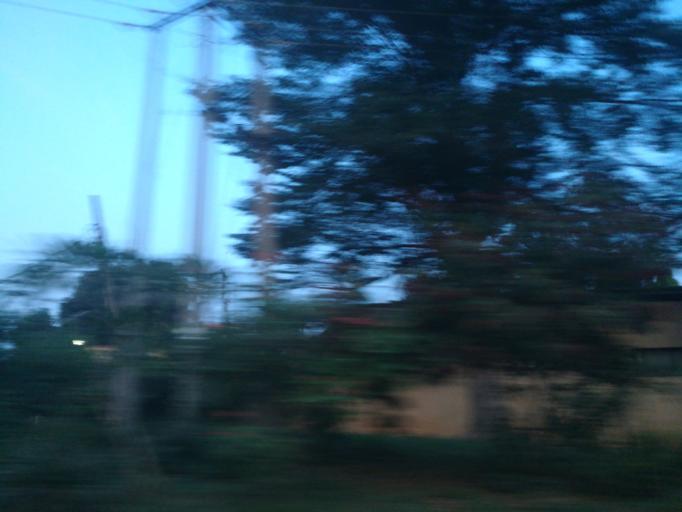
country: NG
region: Abuja Federal Capital Territory
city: Abuja
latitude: 9.0731
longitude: 7.4037
